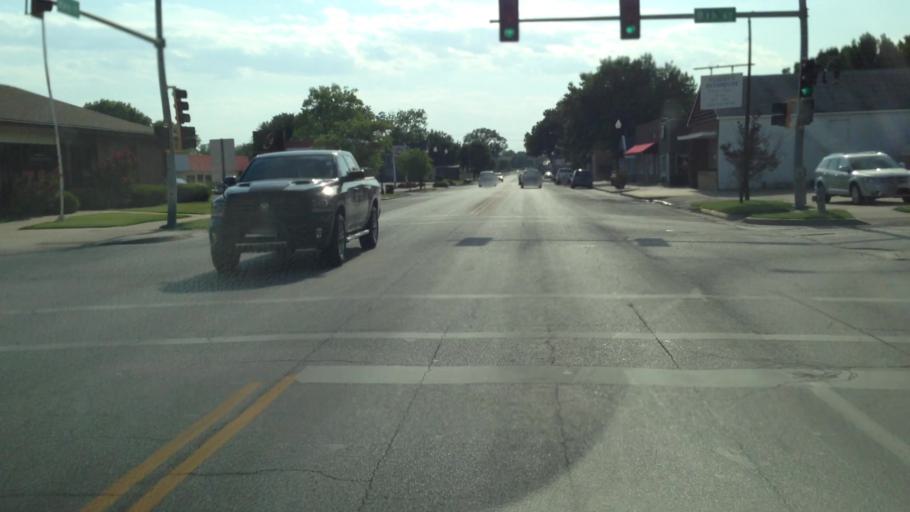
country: US
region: Kansas
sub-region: Wilson County
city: Neodesha
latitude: 37.4175
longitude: -95.6835
